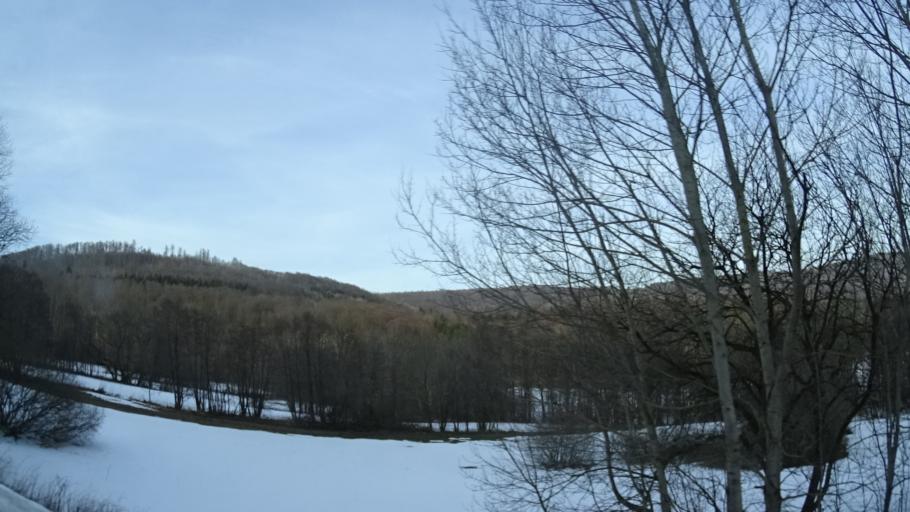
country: DE
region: Bavaria
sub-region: Regierungsbezirk Unterfranken
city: Wildflecken
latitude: 50.3572
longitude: 9.9406
